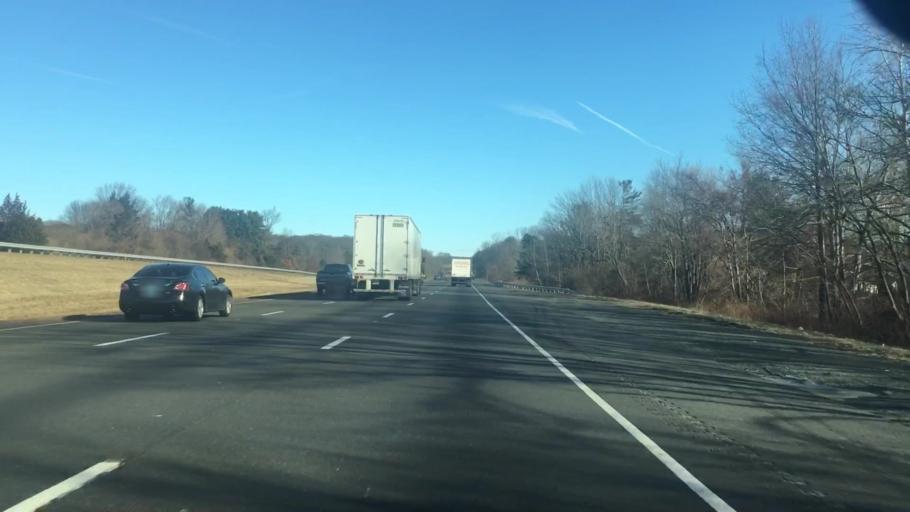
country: US
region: Connecticut
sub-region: New Haven County
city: Wallingford Center
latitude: 41.4396
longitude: -72.7952
